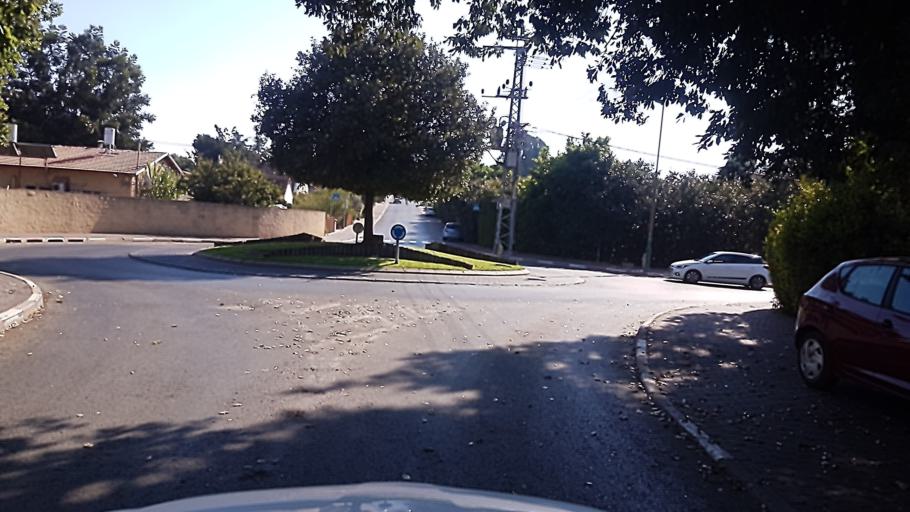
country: IL
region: Central District
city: Kfar Saba
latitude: 32.2098
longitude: 34.9045
